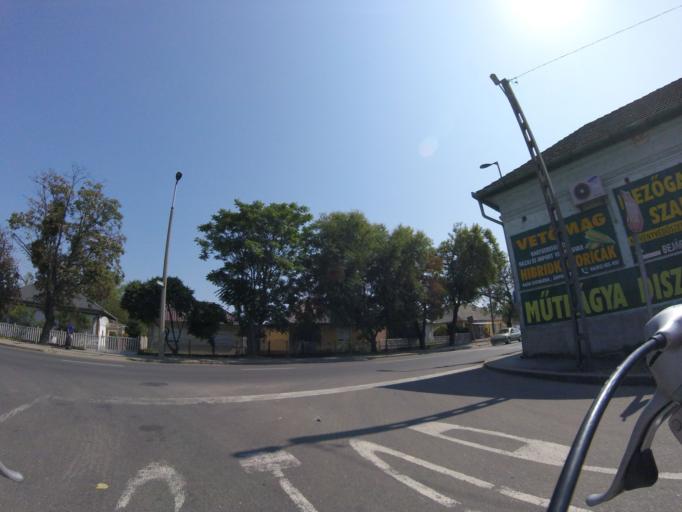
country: HU
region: Szabolcs-Szatmar-Bereg
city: Kisvarda
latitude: 48.2111
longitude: 22.0862
